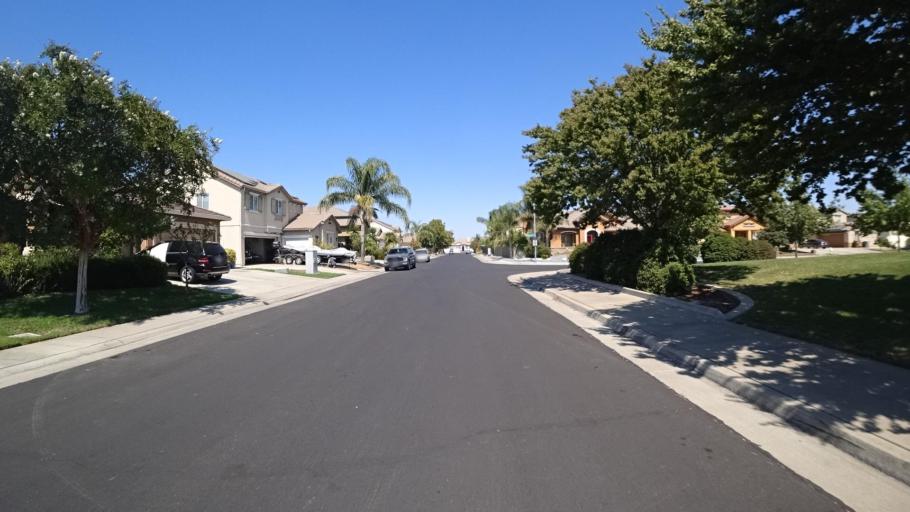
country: US
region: California
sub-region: Sacramento County
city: Elk Grove
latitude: 38.4426
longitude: -121.3897
